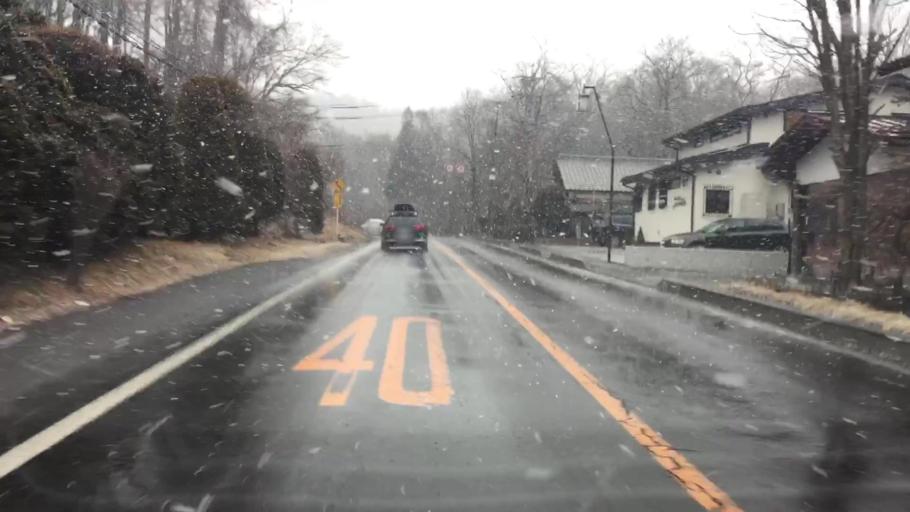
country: JP
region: Nagano
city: Komoro
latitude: 36.3564
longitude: 138.5899
